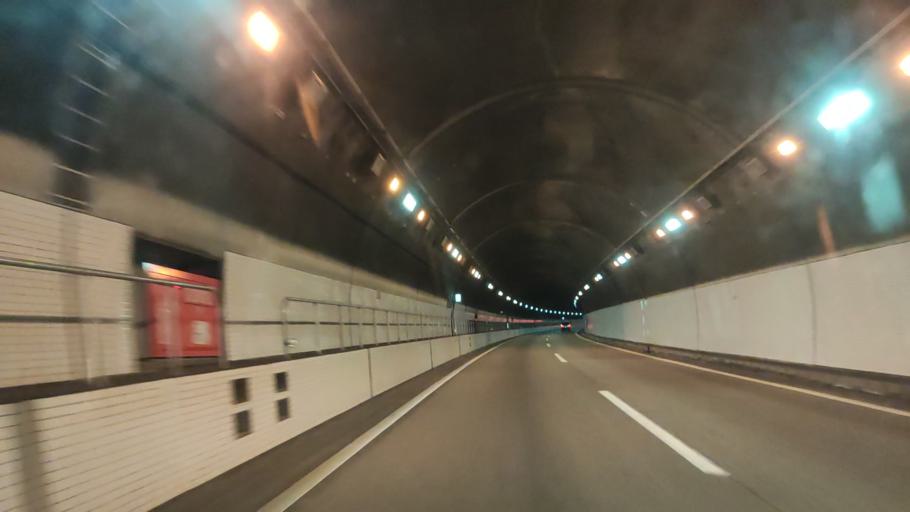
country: JP
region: Ehime
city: Niihama
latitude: 33.9165
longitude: 133.3098
